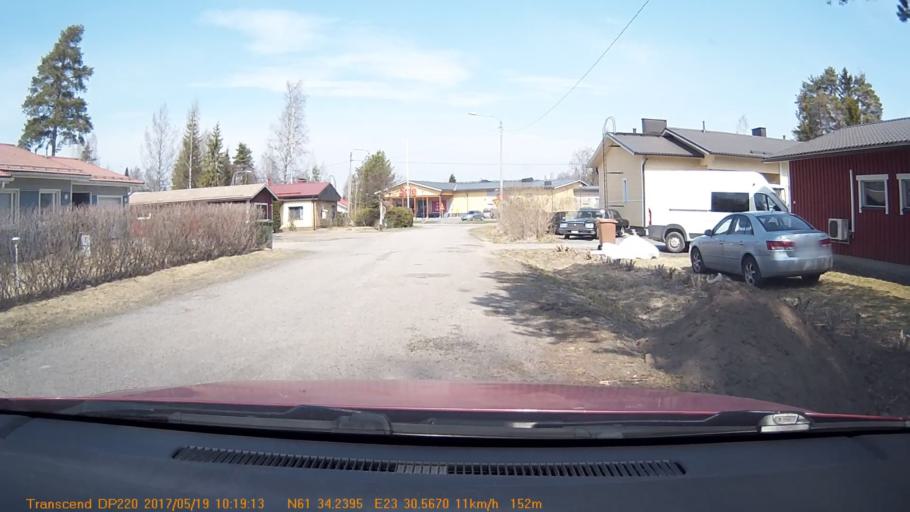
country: FI
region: Pirkanmaa
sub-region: Tampere
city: Yloejaervi
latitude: 61.5708
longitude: 23.5095
